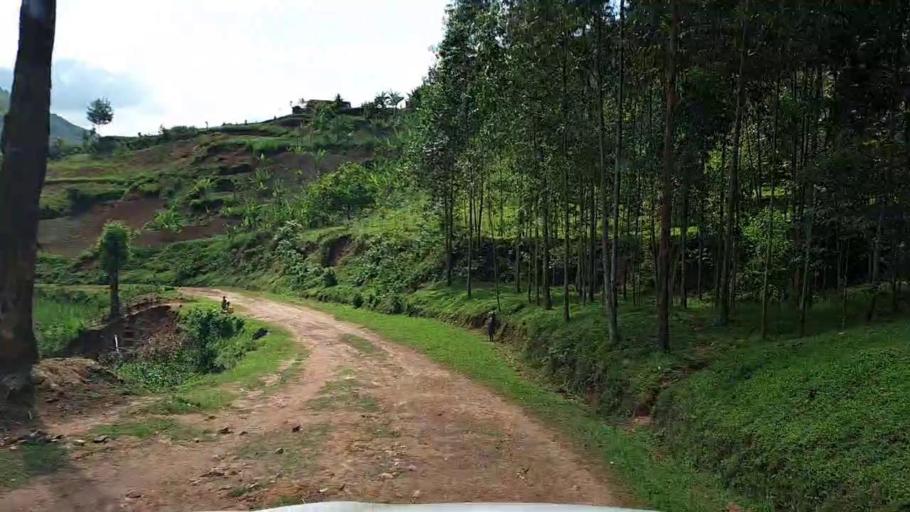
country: RW
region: Southern Province
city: Gikongoro
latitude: -2.3599
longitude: 29.5440
